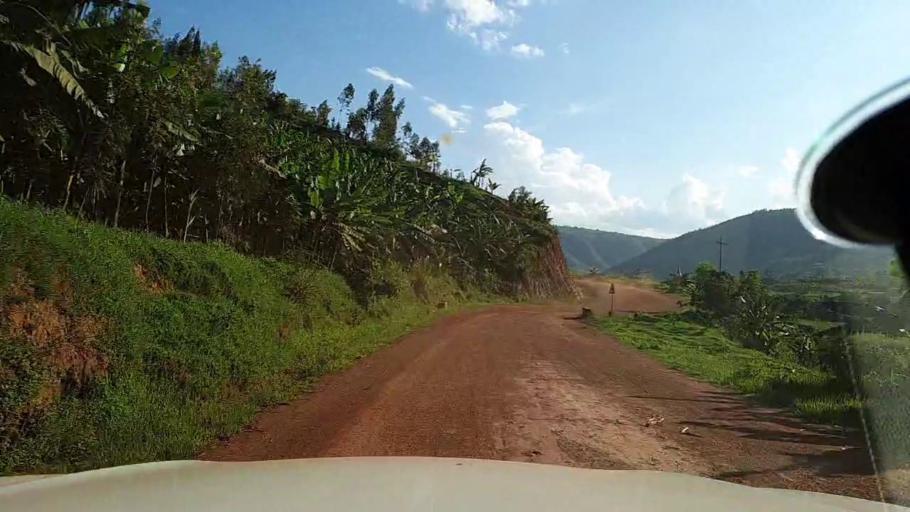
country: RW
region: Kigali
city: Kigali
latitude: -1.8685
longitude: 29.9318
